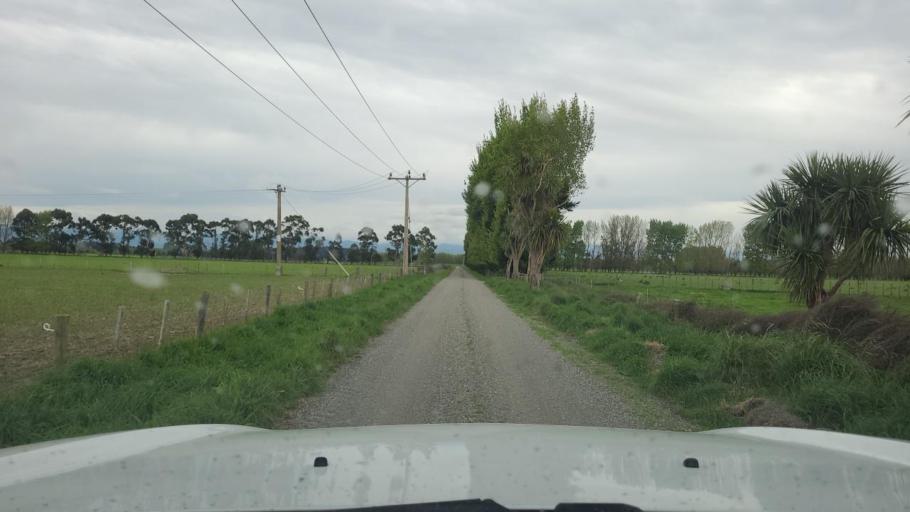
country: NZ
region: Wellington
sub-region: South Wairarapa District
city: Waipawa
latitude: -41.2290
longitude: 175.4010
